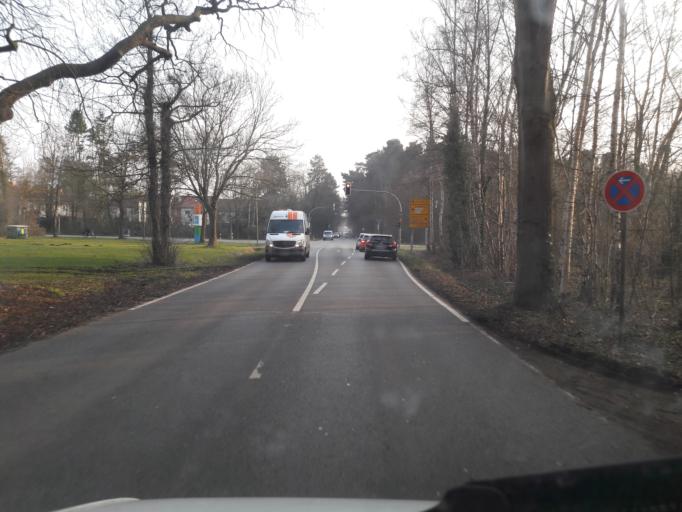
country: DE
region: North Rhine-Westphalia
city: Espelkamp
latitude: 52.3758
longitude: 8.6158
